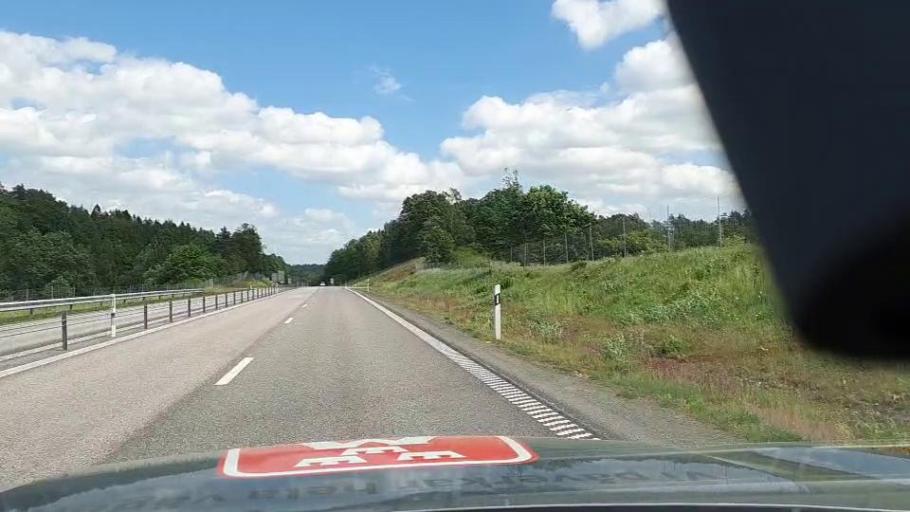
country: SE
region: Blekinge
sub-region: Karlshamns Kommun
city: Karlshamn
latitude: 56.1888
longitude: 14.9357
